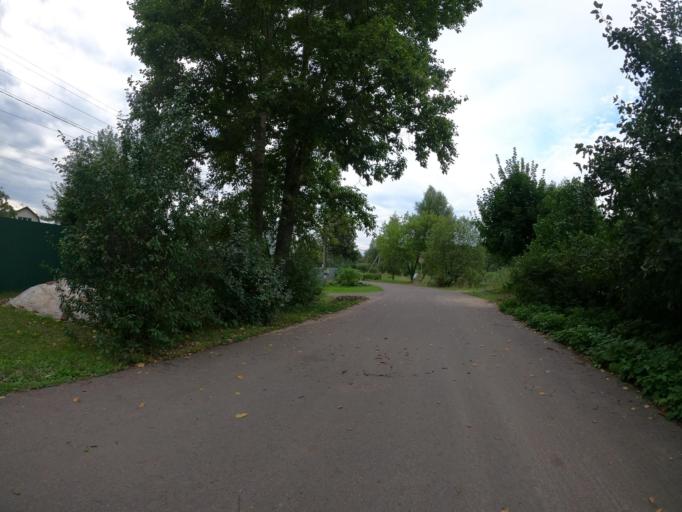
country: RU
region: Moskovskaya
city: Rodniki
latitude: 55.6845
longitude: 38.0965
